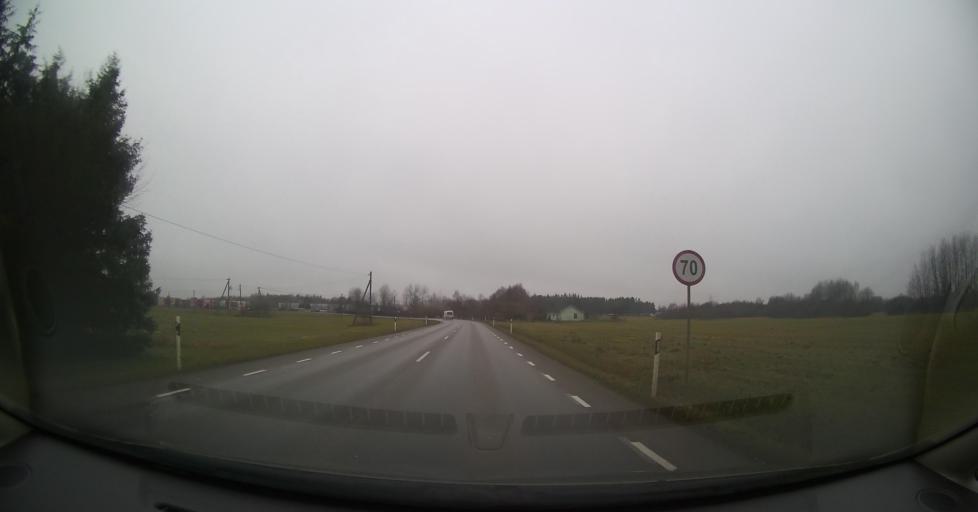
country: EE
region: Tartu
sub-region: Tartu linn
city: Tartu
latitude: 58.3811
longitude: 26.7864
